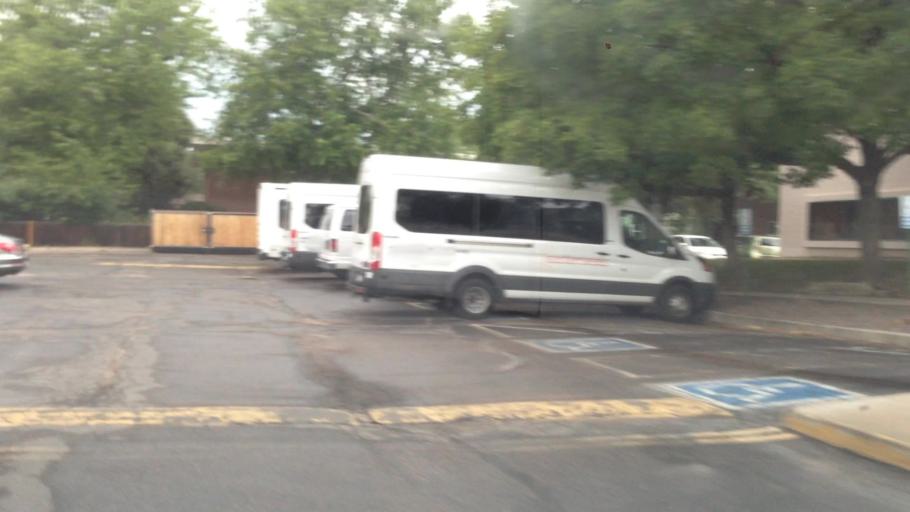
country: US
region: Colorado
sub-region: Jefferson County
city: Lakewood
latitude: 39.7096
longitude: -105.0642
